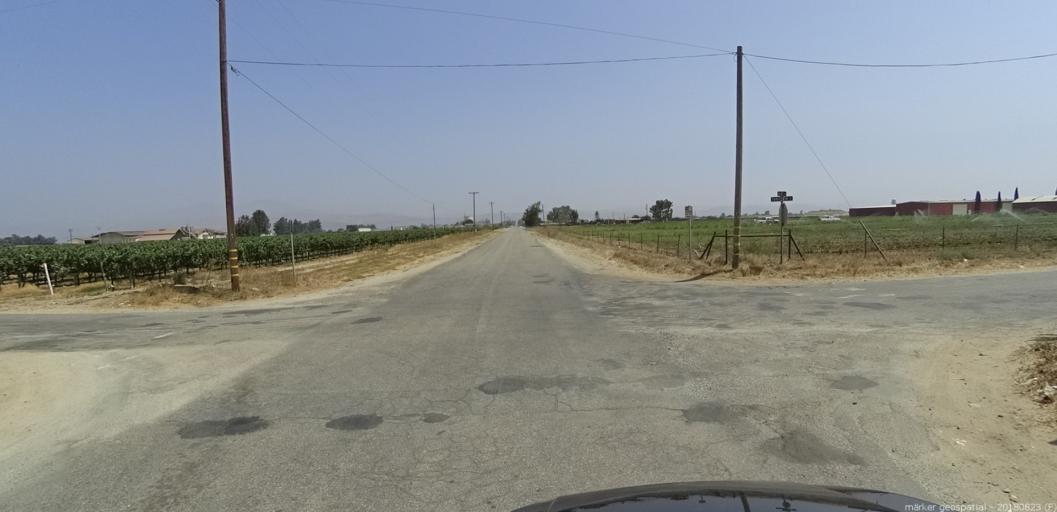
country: US
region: California
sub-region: Monterey County
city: Greenfield
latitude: 36.3185
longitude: -121.2633
